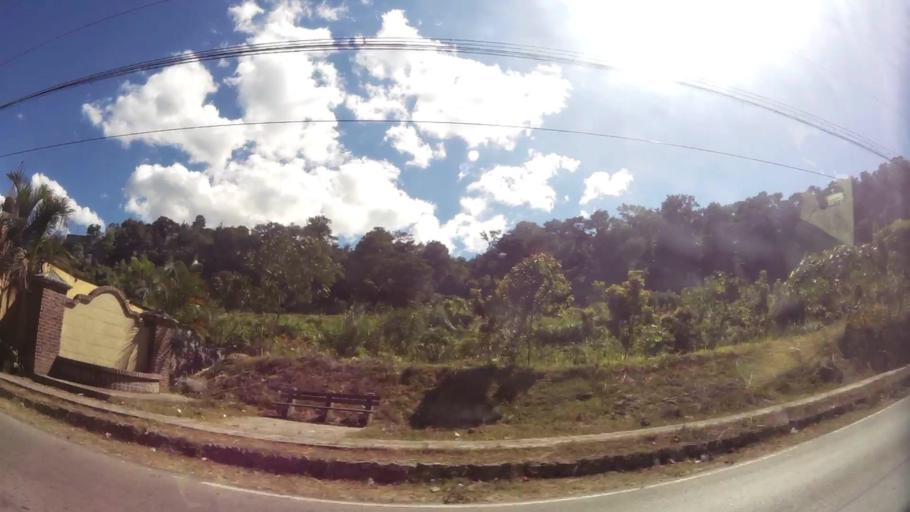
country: GT
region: Guatemala
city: Villa Canales
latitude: 14.4865
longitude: -90.5411
